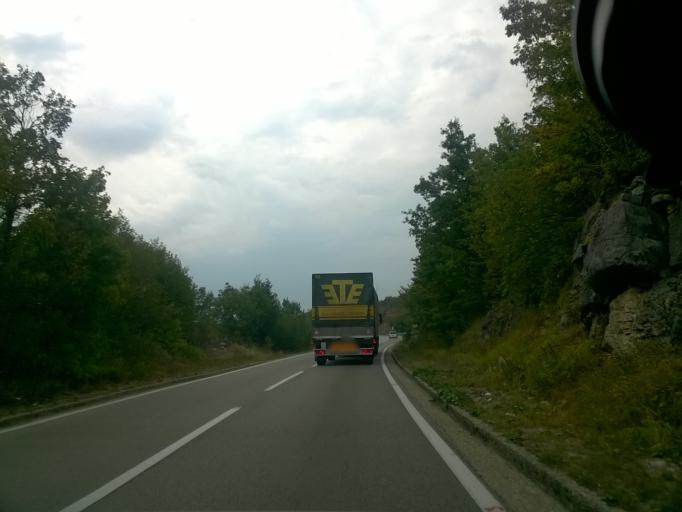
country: ME
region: Kotor
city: Risan
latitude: 42.7530
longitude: 18.6625
